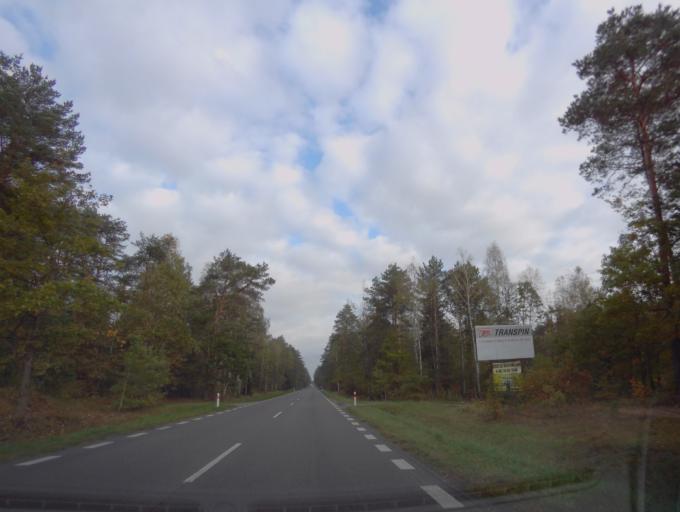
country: PL
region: Lublin Voivodeship
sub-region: Powiat bilgorajski
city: Bilgoraj
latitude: 50.5849
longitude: 22.6839
